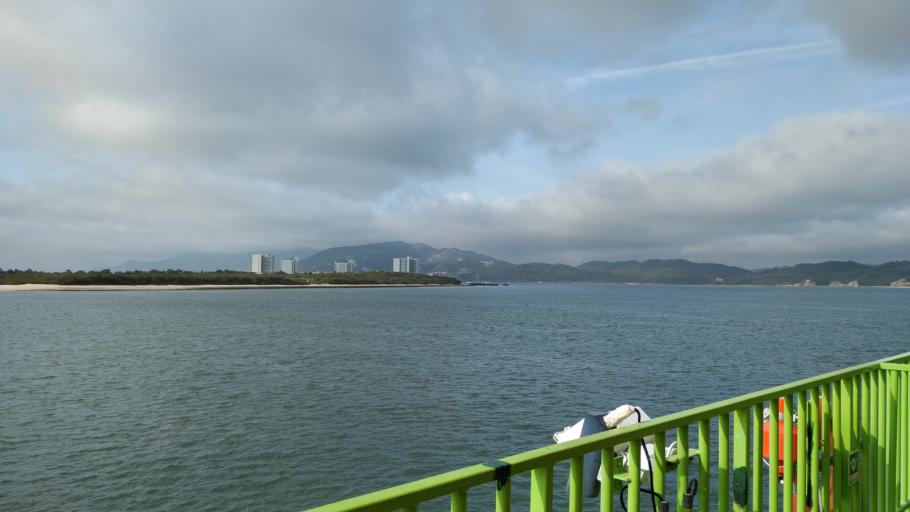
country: PT
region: Setubal
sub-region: Setubal
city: Setubal
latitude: 38.4928
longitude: -8.8831
